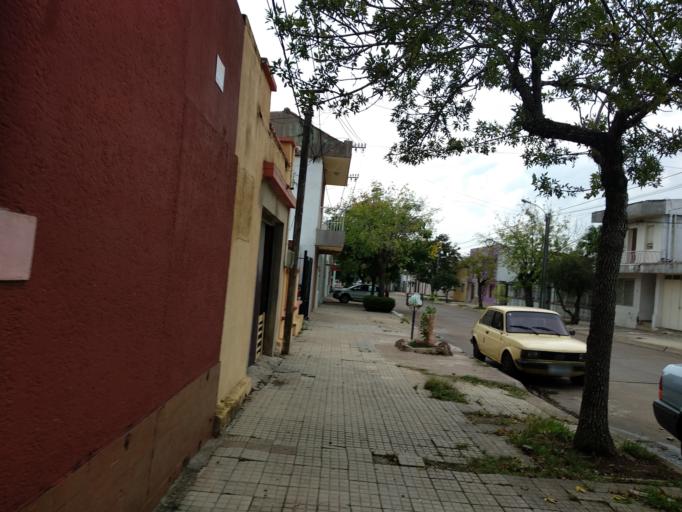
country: UY
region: Artigas
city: Artigas
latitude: -30.4029
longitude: -56.4649
